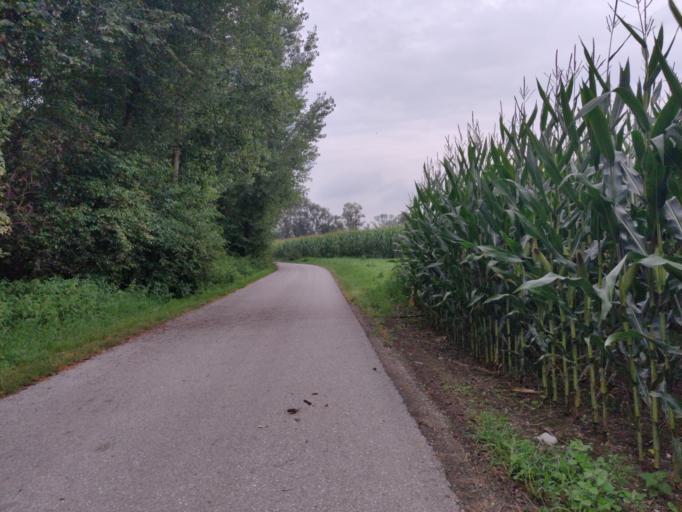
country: AT
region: Upper Austria
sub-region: Politischer Bezirk Linz-Land
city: Enns
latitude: 48.2330
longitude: 14.4565
